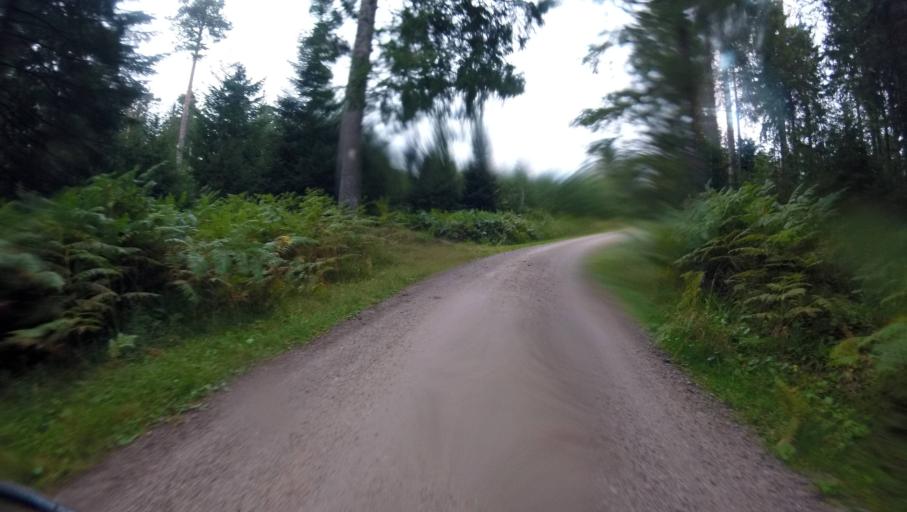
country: DE
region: Baden-Wuerttemberg
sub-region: Karlsruhe Region
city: Weisenbach
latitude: 48.7006
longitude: 8.4068
